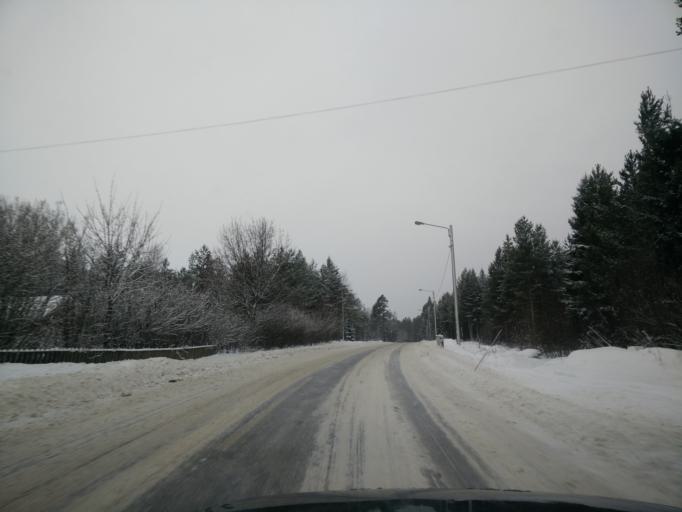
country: SE
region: Jaemtland
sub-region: Braecke Kommun
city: Braecke
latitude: 62.3966
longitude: 15.1977
